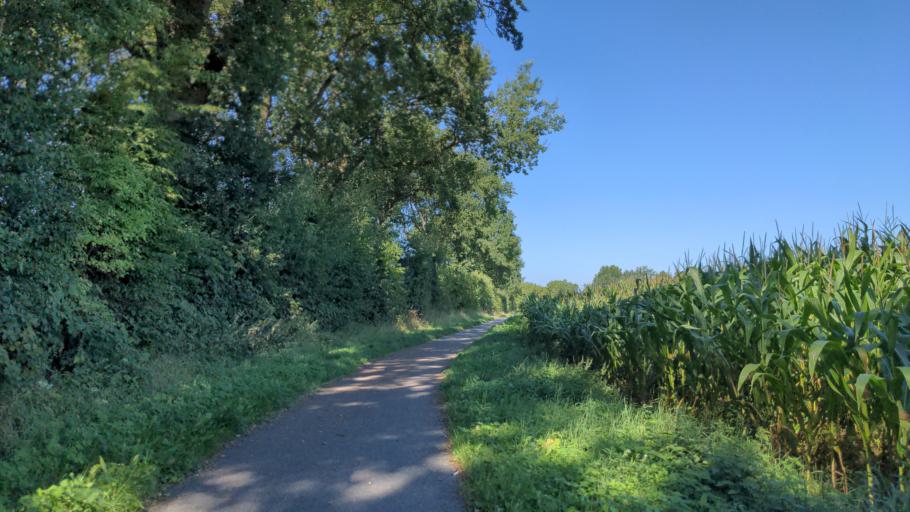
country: DE
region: Schleswig-Holstein
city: Klempau
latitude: 53.7733
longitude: 10.6571
